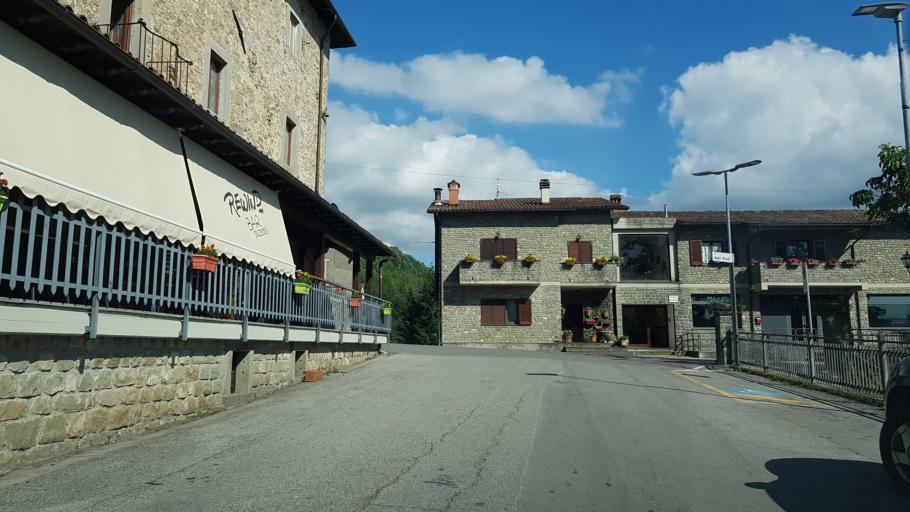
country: IT
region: Tuscany
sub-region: Provincia di Lucca
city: San Romano
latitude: 44.1705
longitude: 10.3469
